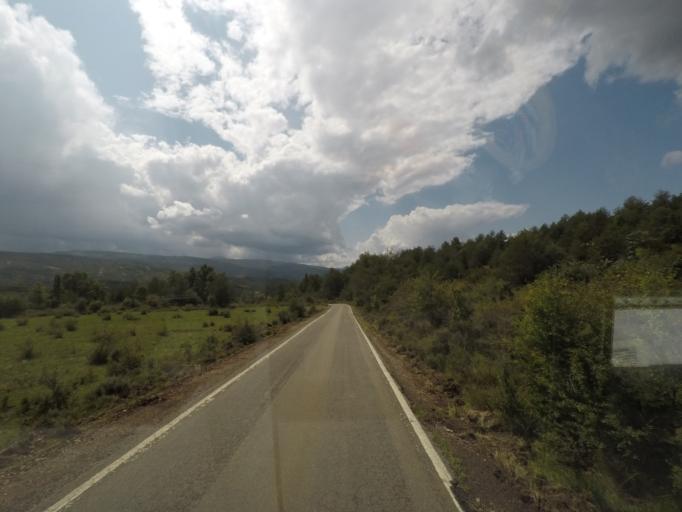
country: ES
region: Aragon
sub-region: Provincia de Huesca
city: Fiscal
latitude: 42.4106
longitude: -0.1307
